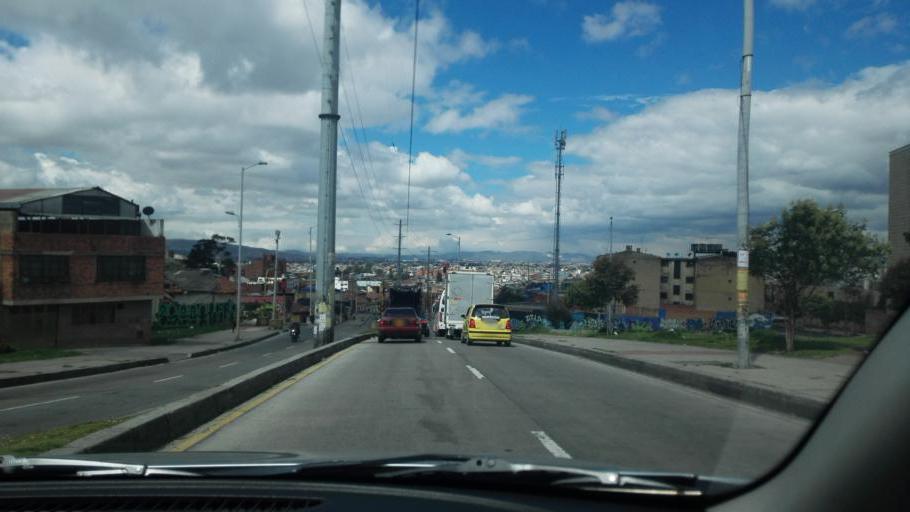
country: CO
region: Bogota D.C.
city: Bogota
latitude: 4.5900
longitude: -74.0767
